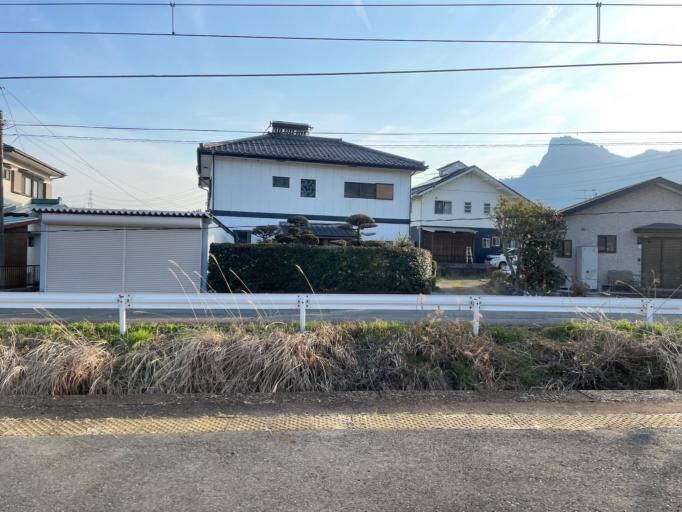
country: JP
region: Gunma
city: Annaka
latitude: 36.3161
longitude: 138.7868
